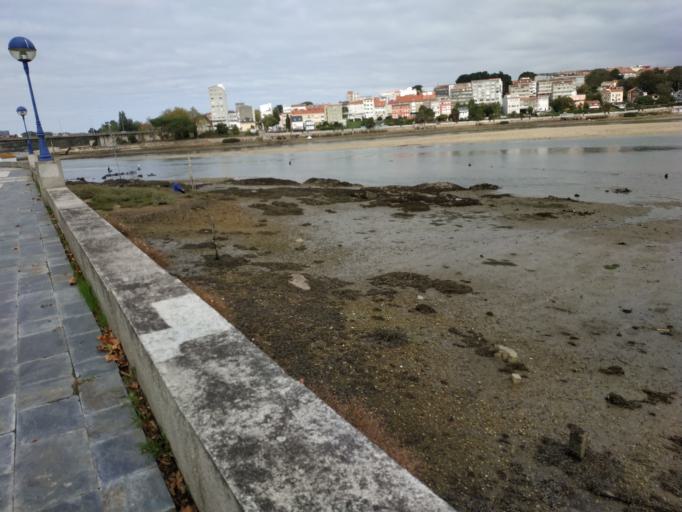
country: ES
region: Galicia
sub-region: Provincia da Coruna
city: Culleredo
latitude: 43.3287
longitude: -8.3792
